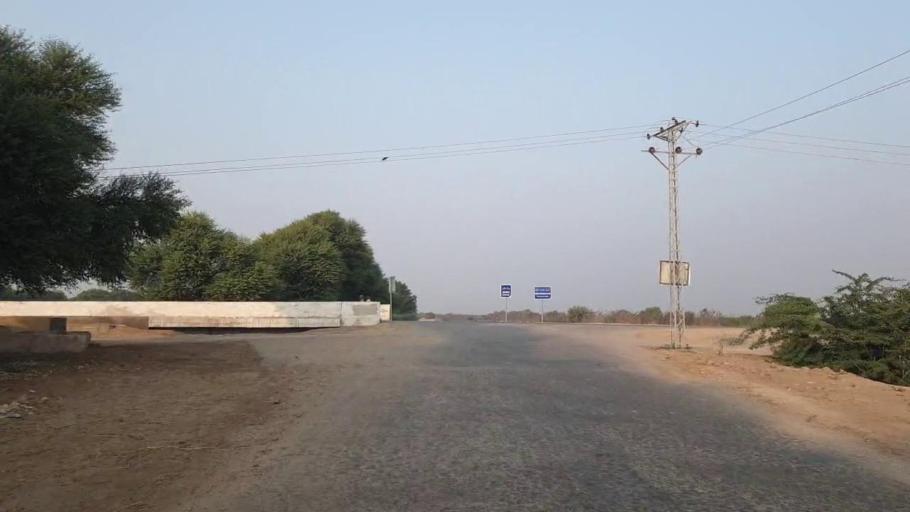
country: PK
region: Sindh
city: Tando Muhammad Khan
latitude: 25.1327
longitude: 68.4346
